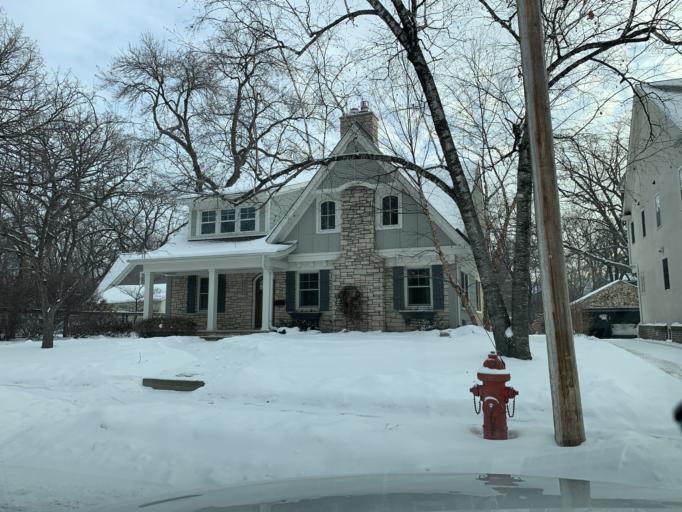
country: US
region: Minnesota
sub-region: Hennepin County
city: Saint Louis Park
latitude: 44.9204
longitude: -93.3519
